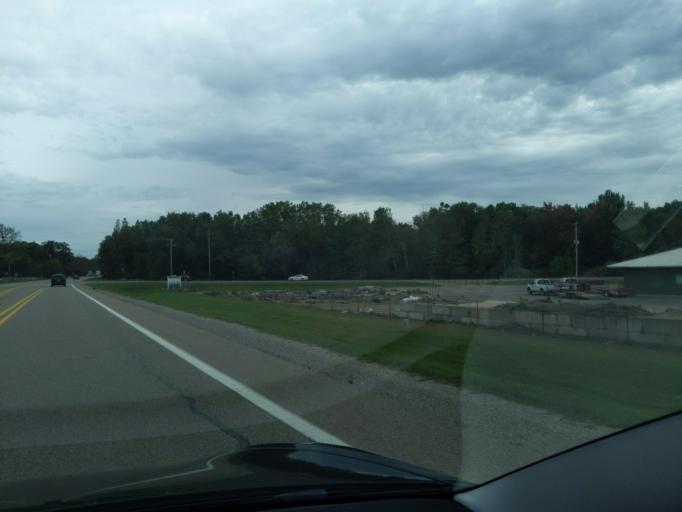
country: US
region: Michigan
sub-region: Clare County
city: Clare
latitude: 43.8585
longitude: -84.9008
